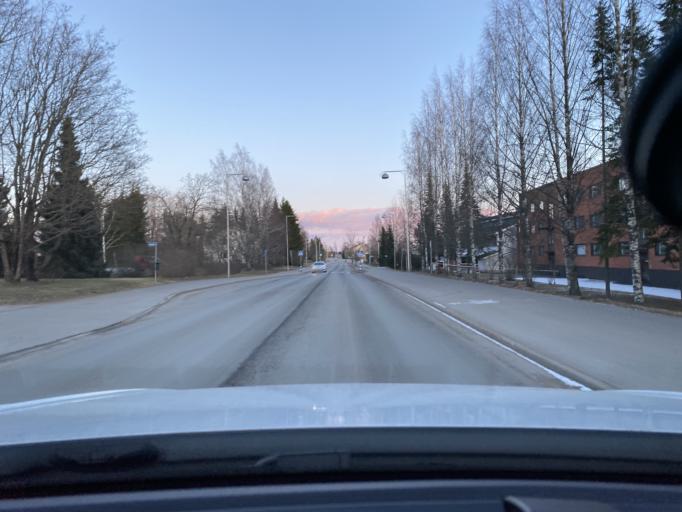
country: FI
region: Pirkanmaa
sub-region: Lounais-Pirkanmaa
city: Punkalaidun
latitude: 61.1139
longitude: 23.0980
